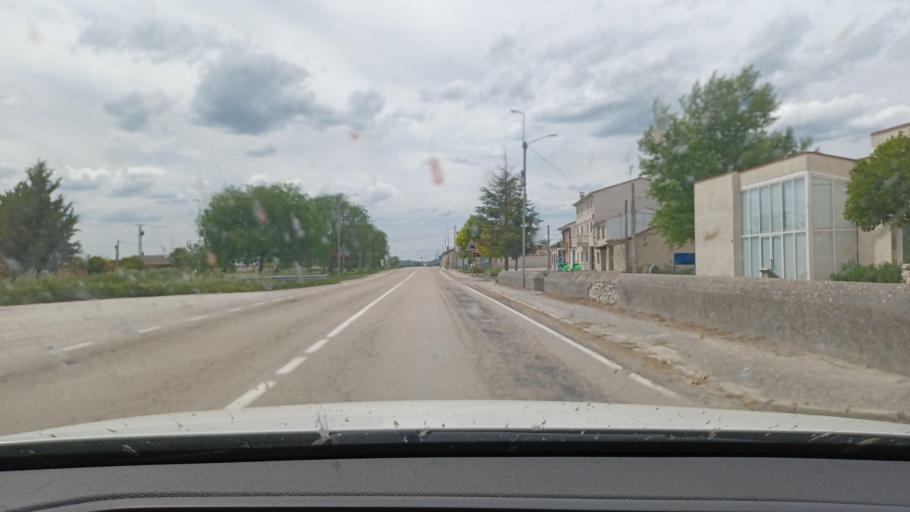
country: ES
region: Castille and Leon
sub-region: Provincia de Segovia
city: Frumales
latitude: 41.3837
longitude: -4.2393
